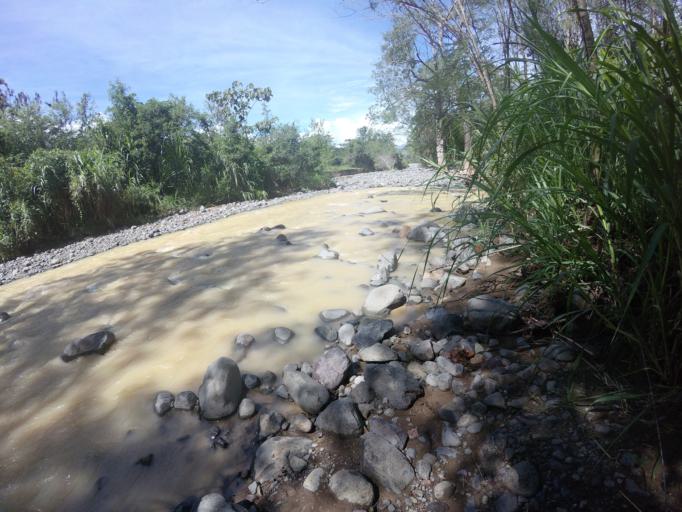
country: CO
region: Antioquia
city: Tarso
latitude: 5.8722
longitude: -75.7596
